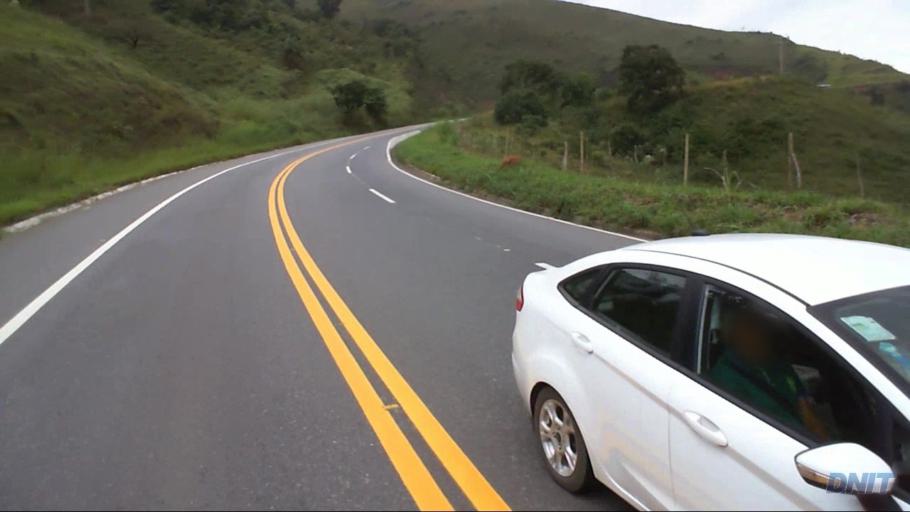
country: BR
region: Minas Gerais
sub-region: Nova Era
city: Nova Era
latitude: -19.6858
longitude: -42.9888
